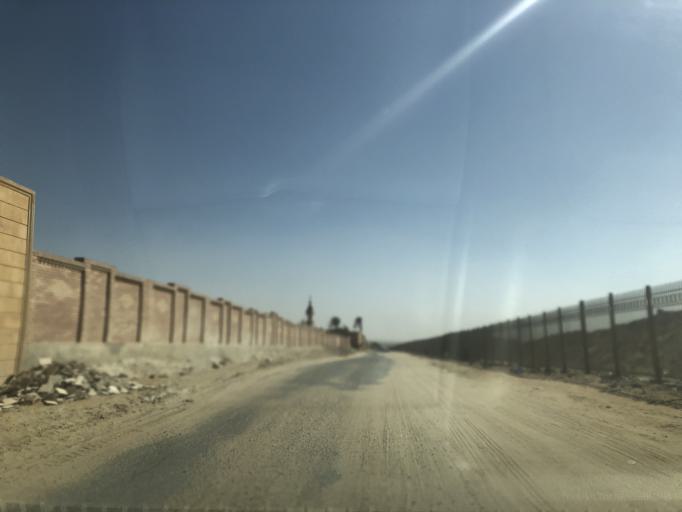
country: EG
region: Al Jizah
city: Madinat Sittah Uktubar
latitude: 29.9324
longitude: 30.9550
